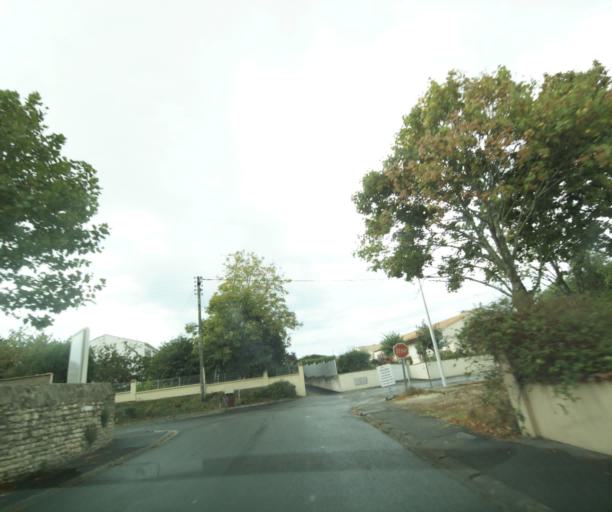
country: FR
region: Poitou-Charentes
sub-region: Departement de la Charente-Maritime
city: Tonnay-Charente
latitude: 45.9460
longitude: -0.8817
